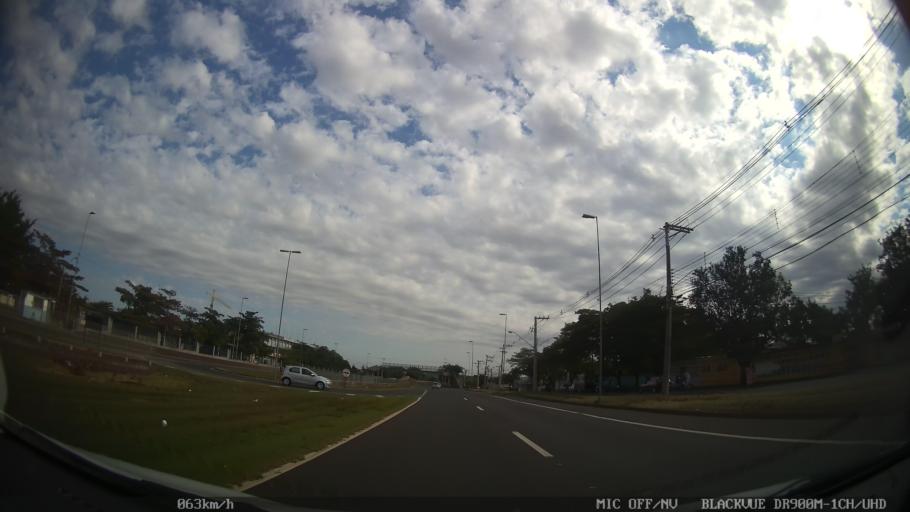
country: BR
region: Sao Paulo
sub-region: Limeira
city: Limeira
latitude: -22.5682
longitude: -47.4434
